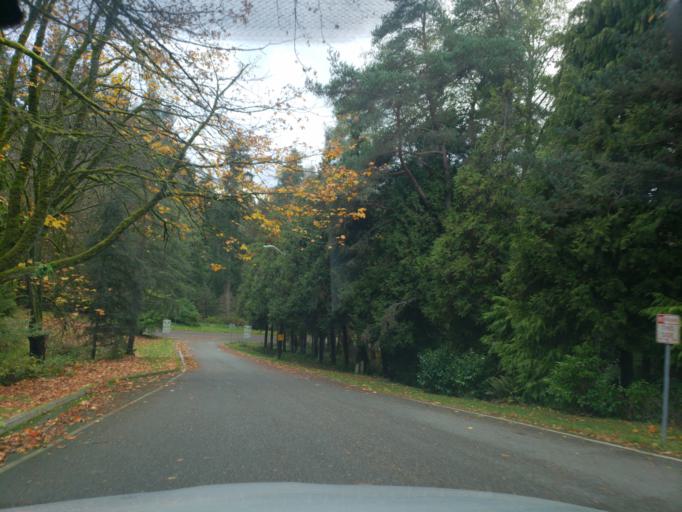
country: US
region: Washington
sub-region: Snohomish County
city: Everett
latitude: 47.9600
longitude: -122.2234
